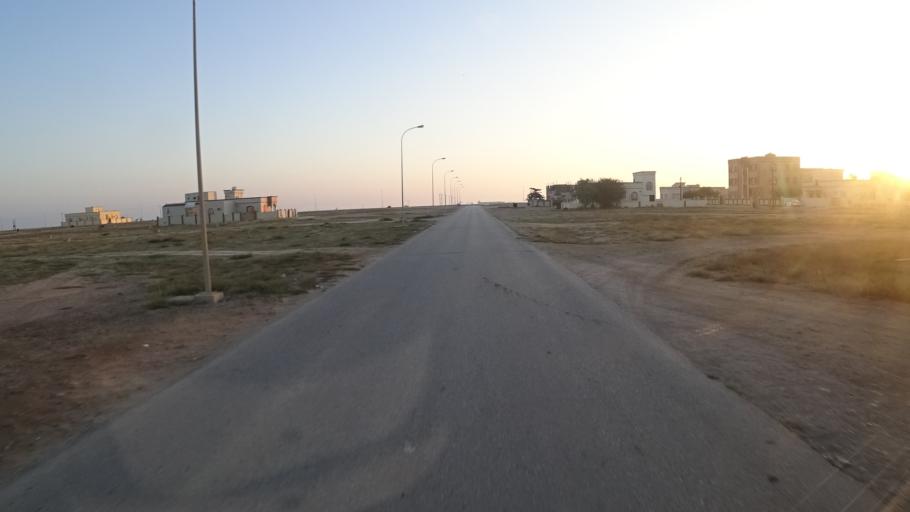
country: OM
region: Zufar
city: Salalah
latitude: 16.9817
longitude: 54.7104
